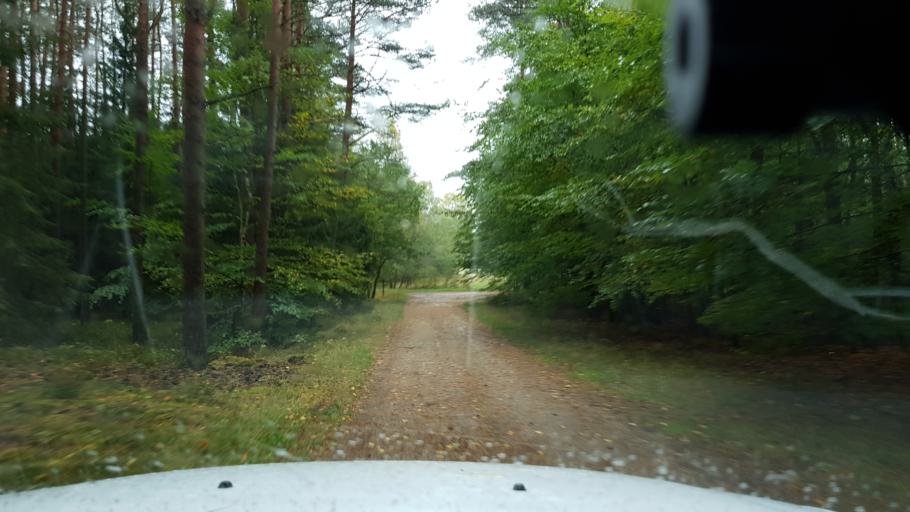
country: PL
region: West Pomeranian Voivodeship
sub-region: Powiat goleniowski
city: Przybiernow
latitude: 53.7269
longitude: 14.8113
